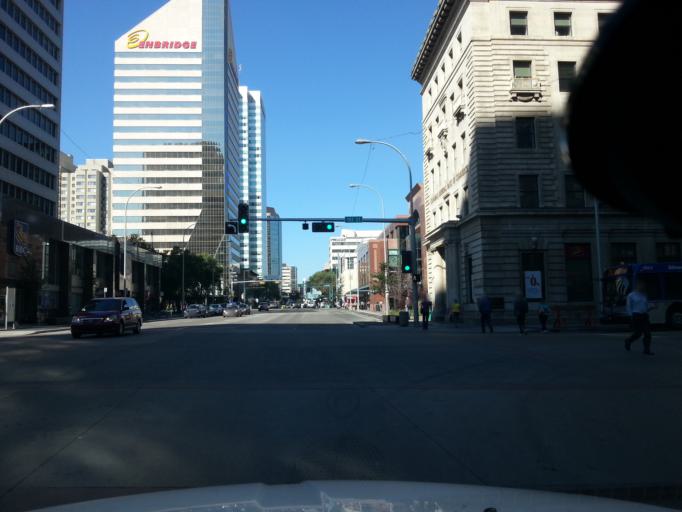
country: CA
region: Alberta
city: Edmonton
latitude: 53.5410
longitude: -113.4934
